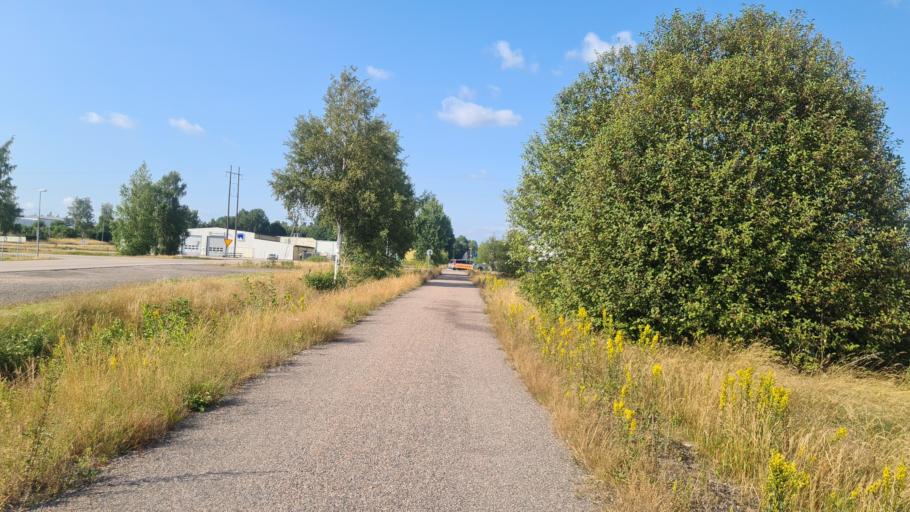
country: SE
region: Kronoberg
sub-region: Ljungby Kommun
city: Ljungby
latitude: 56.8172
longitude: 13.9192
